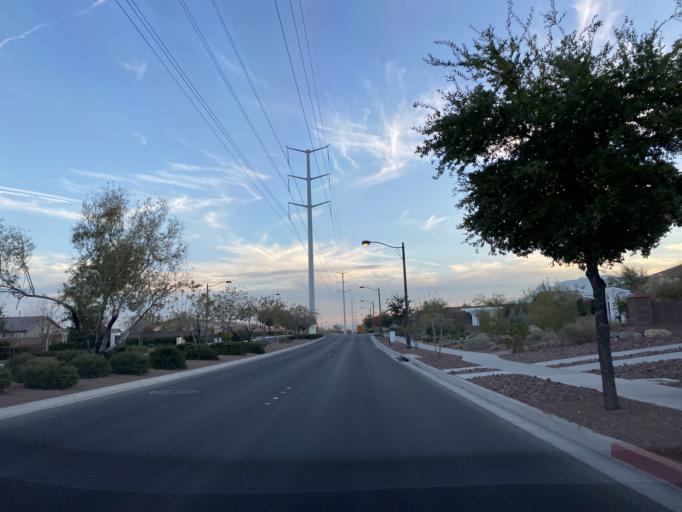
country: US
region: Nevada
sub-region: Clark County
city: Summerlin South
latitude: 36.2924
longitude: -115.3289
